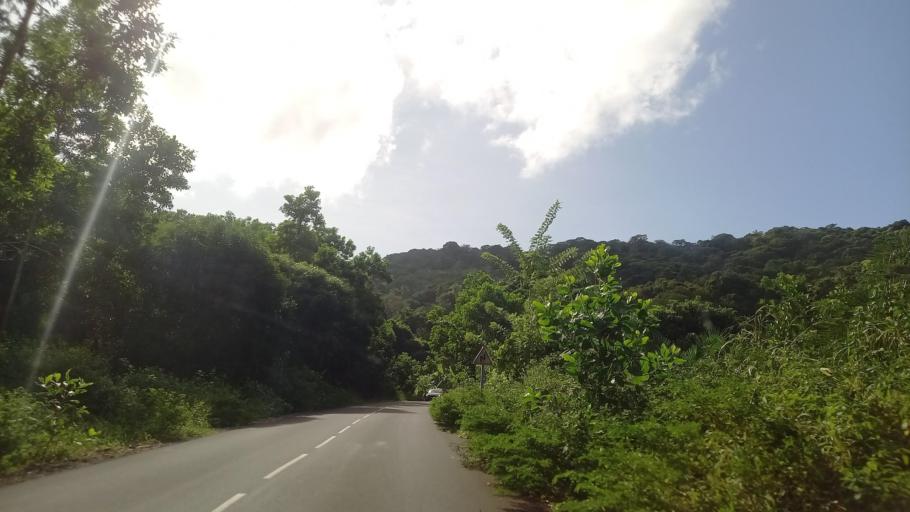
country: YT
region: Kani-Keli
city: Kani Keli
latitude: -12.9863
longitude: 45.1401
